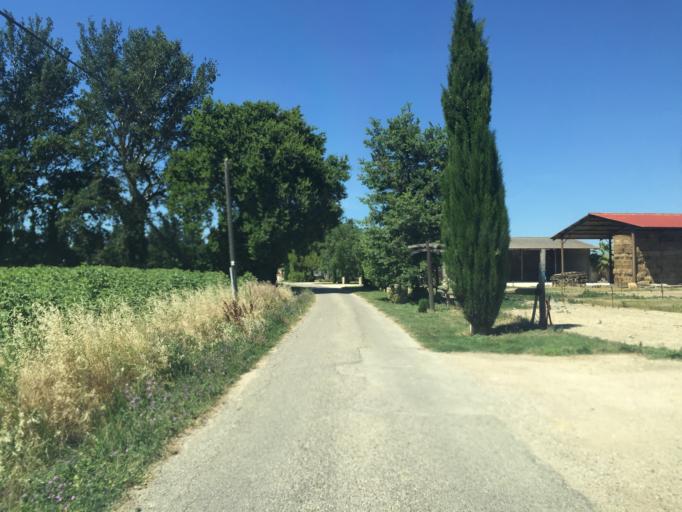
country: FR
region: Provence-Alpes-Cote d'Azur
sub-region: Departement du Vaucluse
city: Courthezon
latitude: 44.0714
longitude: 4.9157
